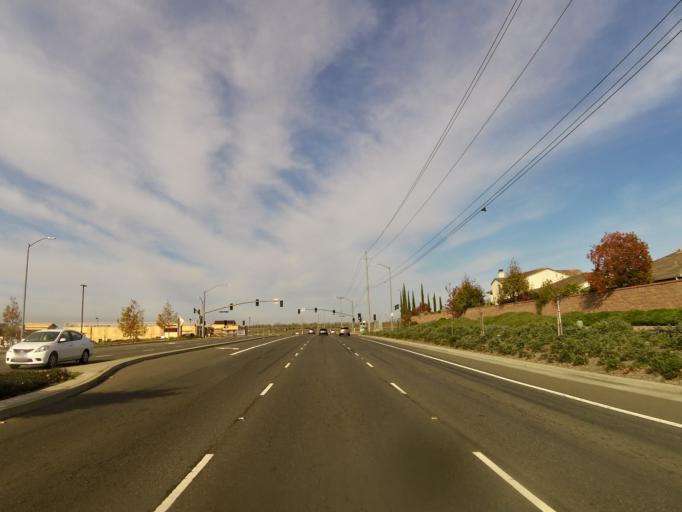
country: US
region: California
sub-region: Sacramento County
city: Rancho Cordova
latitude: 38.5555
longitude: -121.2428
